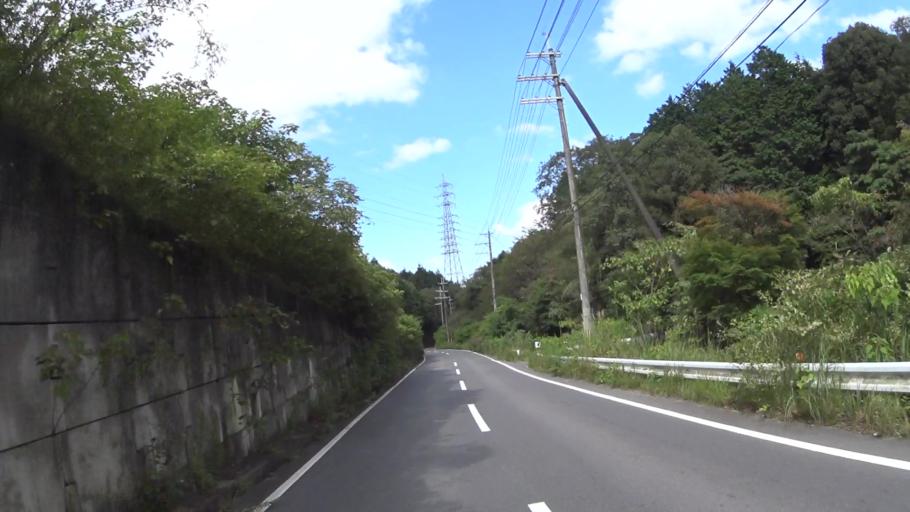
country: JP
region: Shiga Prefecture
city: Otsu-shi
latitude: 34.9351
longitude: 135.8895
